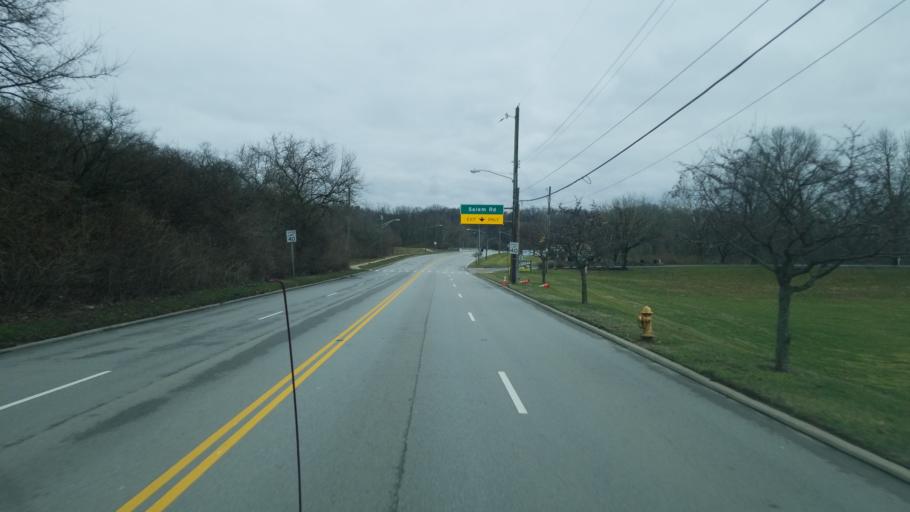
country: US
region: Kentucky
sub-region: Campbell County
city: Fort Thomas
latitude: 39.0885
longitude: -84.4237
